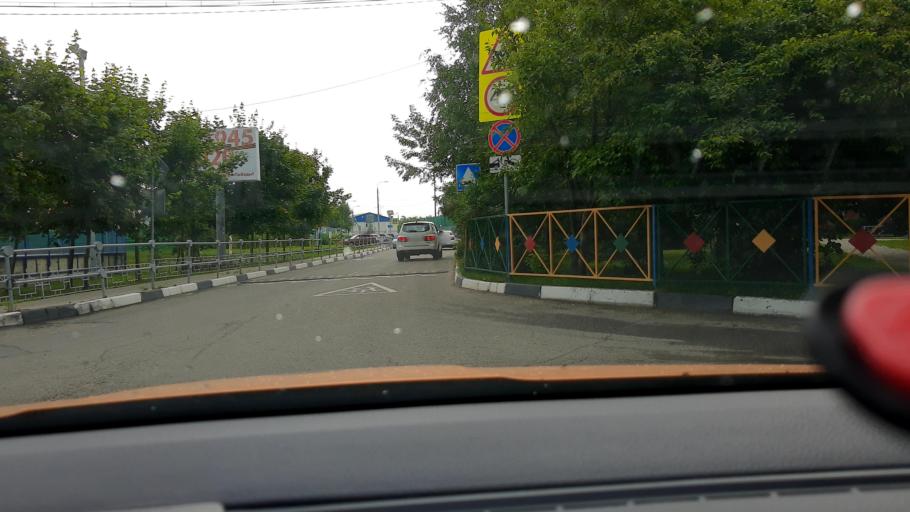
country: RU
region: Moskovskaya
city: Gorki Vtoryye
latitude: 55.7249
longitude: 37.1656
